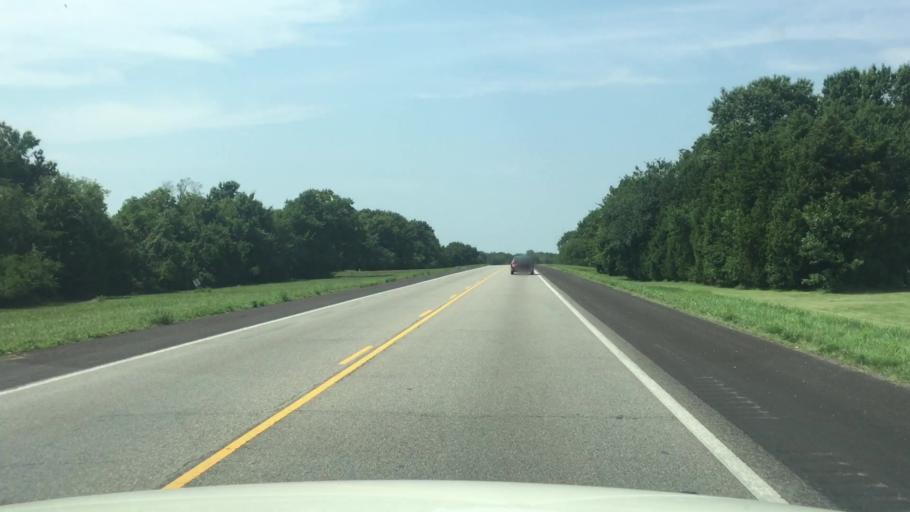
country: US
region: Kansas
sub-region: Crawford County
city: Pittsburg
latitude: 37.3883
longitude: -94.7122
